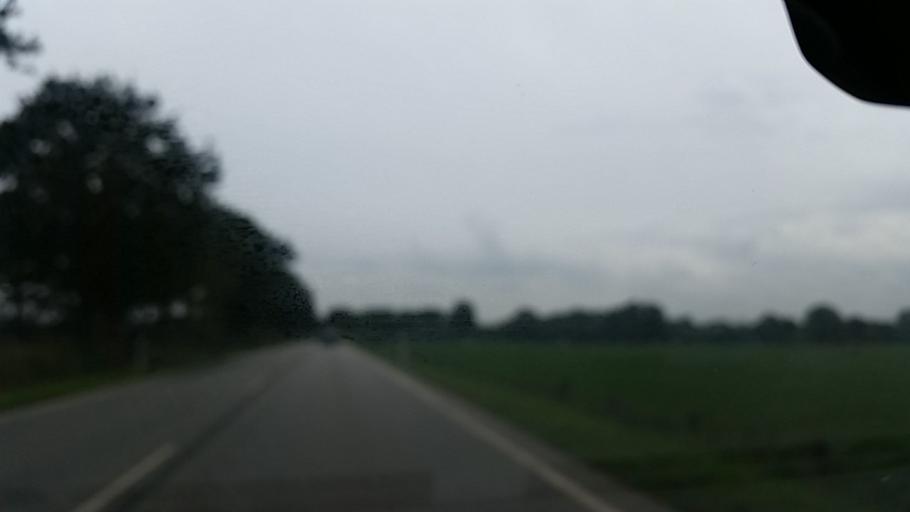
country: DE
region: Schleswig-Holstein
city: Kayhude
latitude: 53.7826
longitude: 10.1296
